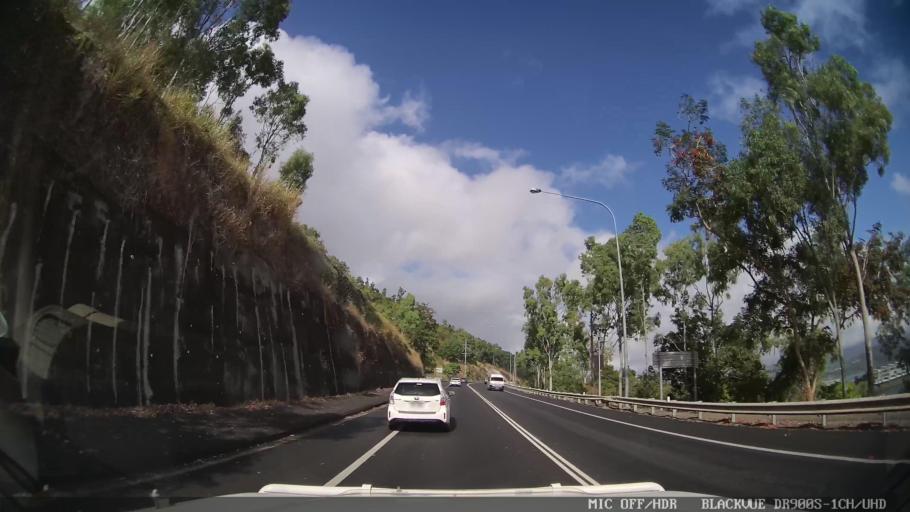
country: AU
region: Queensland
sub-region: Whitsunday
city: Proserpine
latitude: -20.2696
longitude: 148.7109
